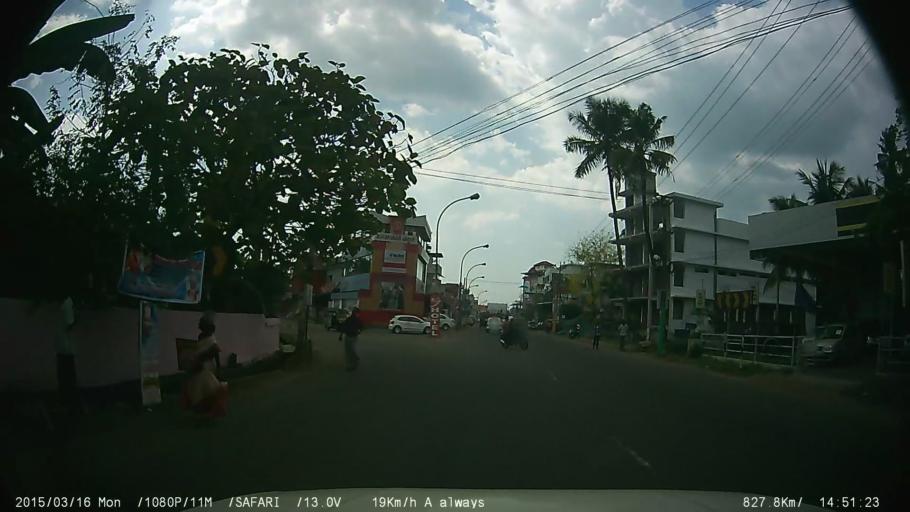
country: IN
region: Kerala
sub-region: Ernakulam
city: Angamali
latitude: 10.1884
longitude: 76.3931
